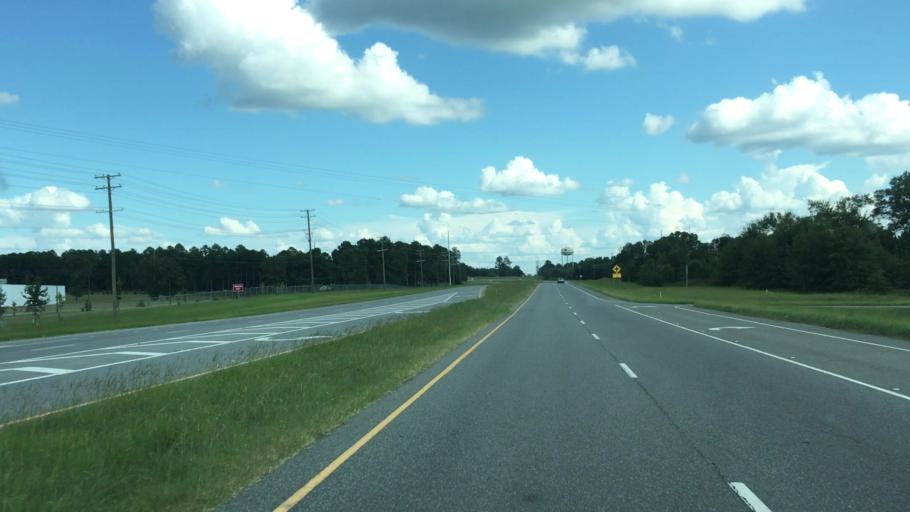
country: US
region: Georgia
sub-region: Laurens County
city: Dublin
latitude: 32.5070
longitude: -82.9465
